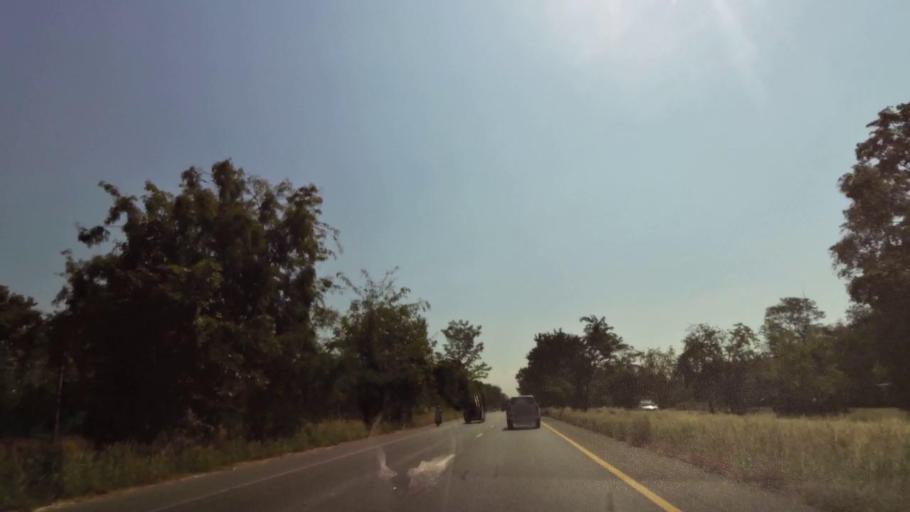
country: TH
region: Nakhon Sawan
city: Kao Liao
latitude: 15.8523
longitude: 100.1172
